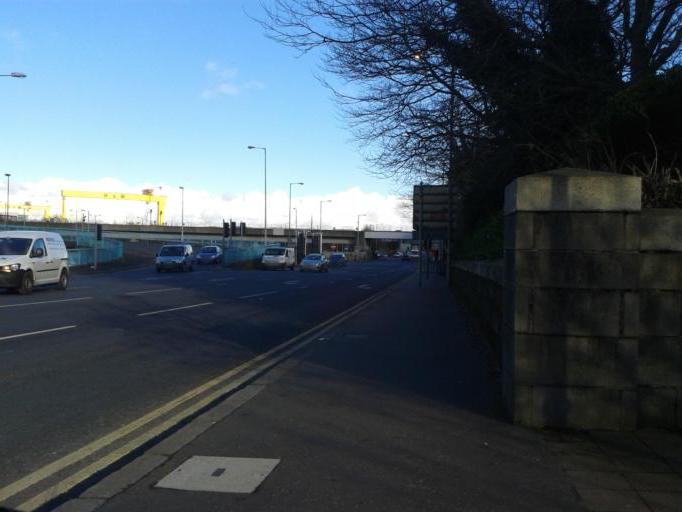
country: GB
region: Northern Ireland
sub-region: City of Belfast
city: Belfast
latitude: 54.5997
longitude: -5.9192
